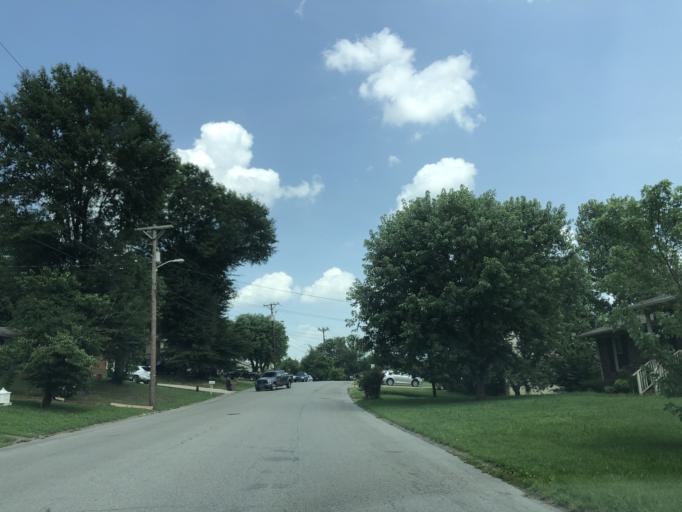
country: US
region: Tennessee
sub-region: Williamson County
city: Brentwood Estates
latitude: 36.0577
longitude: -86.6930
